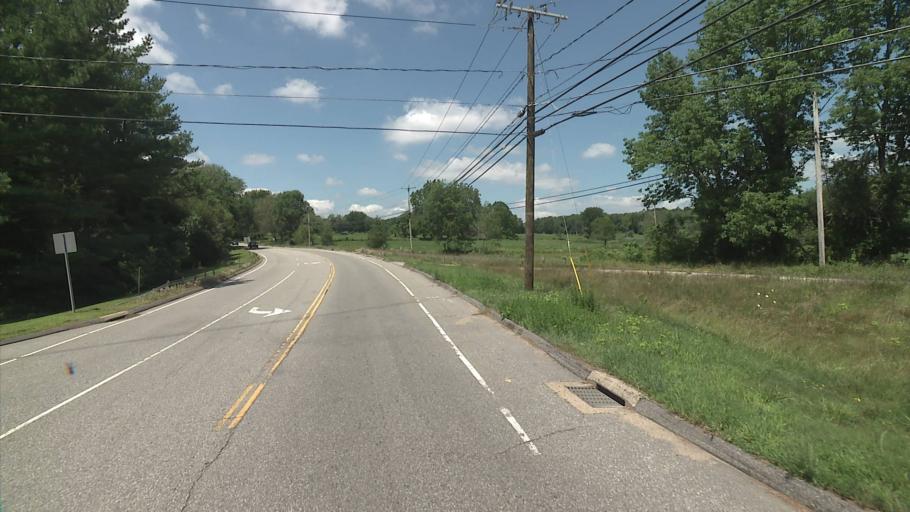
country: US
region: Connecticut
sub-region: Windham County
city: Windham
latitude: 41.7007
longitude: -72.1444
